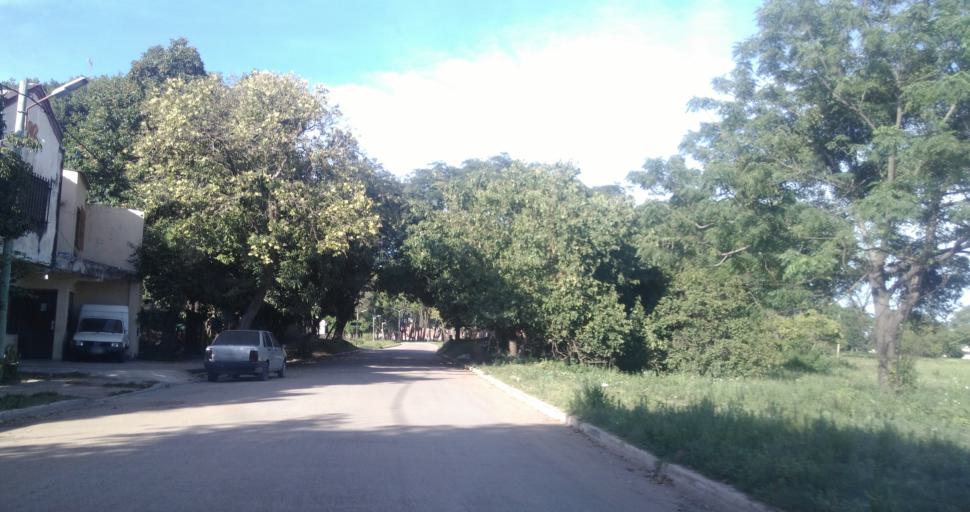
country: AR
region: Chaco
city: Fontana
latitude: -27.4146
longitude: -59.0279
